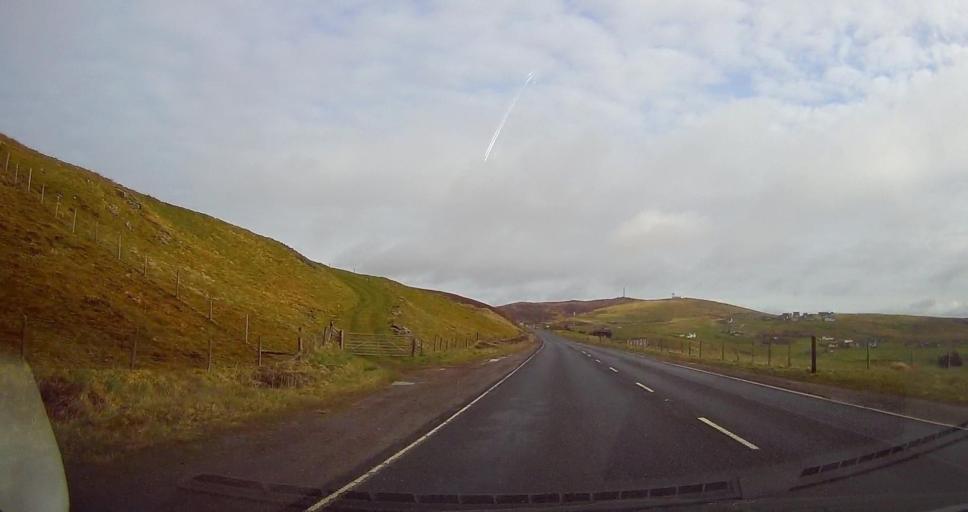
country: GB
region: Scotland
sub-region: Shetland Islands
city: Lerwick
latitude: 60.1285
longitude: -1.2158
